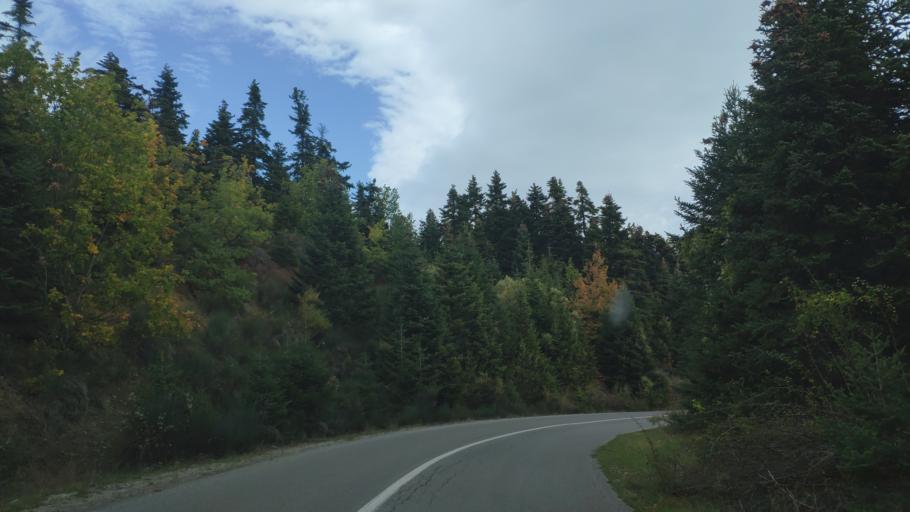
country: GR
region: Central Greece
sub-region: Nomos Fthiotidos
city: Stavros
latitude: 38.7188
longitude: 22.3265
